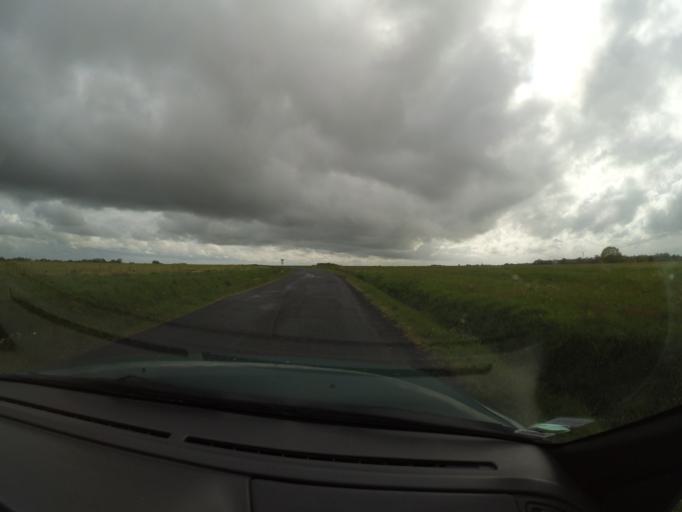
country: FR
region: Pays de la Loire
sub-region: Departement de la Loire-Atlantique
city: Maisdon-sur-Sevre
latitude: 47.0907
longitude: -1.3705
